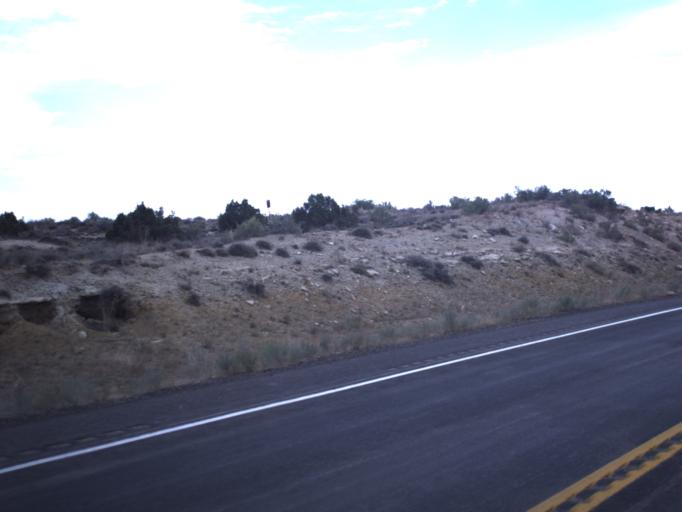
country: US
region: Utah
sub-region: Uintah County
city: Naples
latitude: 40.1930
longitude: -109.3316
